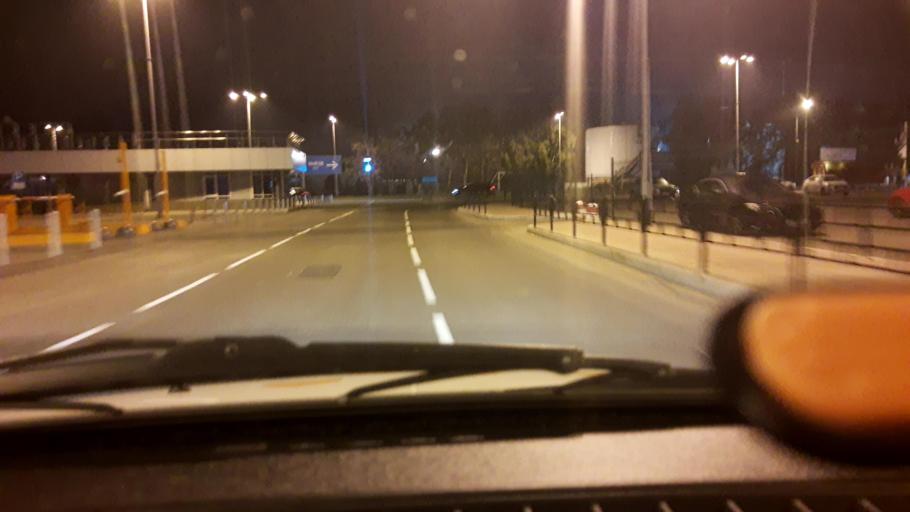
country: RU
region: Bashkortostan
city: Ufa
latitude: 54.5667
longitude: 55.8852
